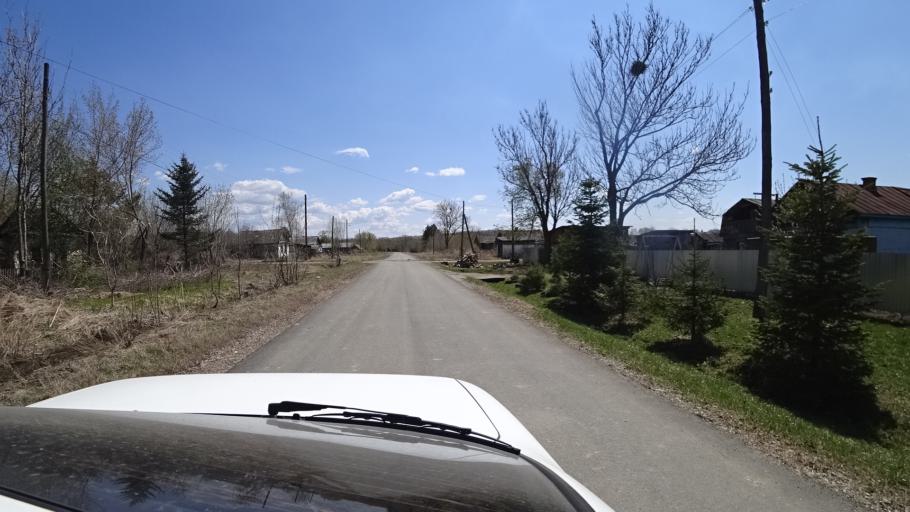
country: RU
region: Primorskiy
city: Dal'nerechensk
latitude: 45.7924
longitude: 133.7697
